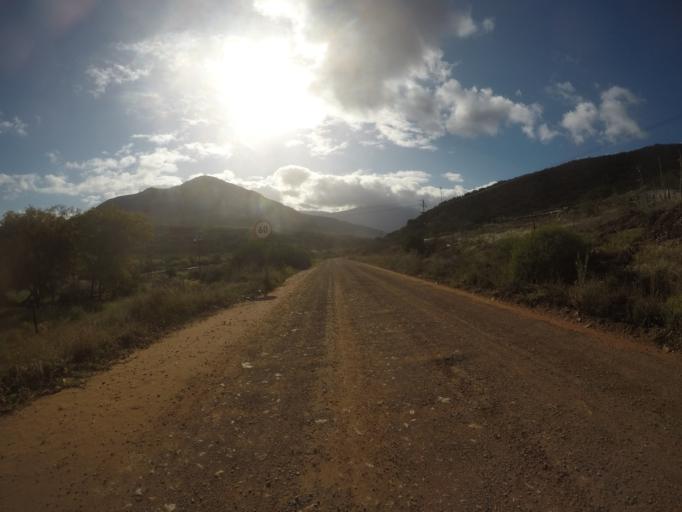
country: ZA
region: Western Cape
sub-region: West Coast District Municipality
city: Clanwilliam
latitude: -32.3635
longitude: 18.9427
